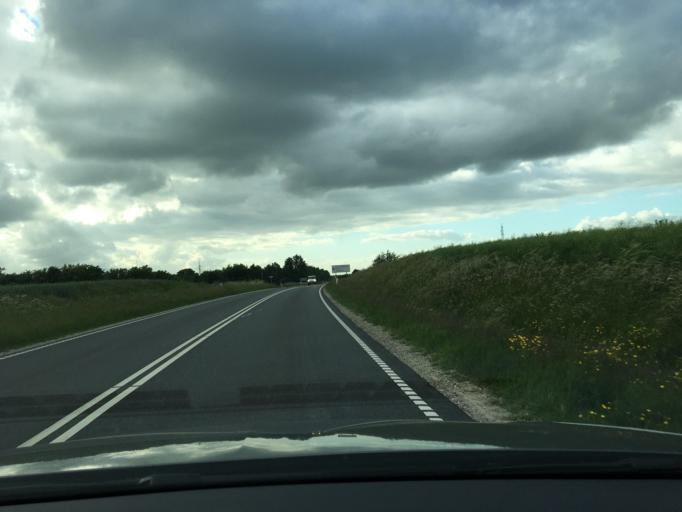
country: DK
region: Central Jutland
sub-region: Arhus Kommune
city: Logten
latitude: 56.2943
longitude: 10.2849
